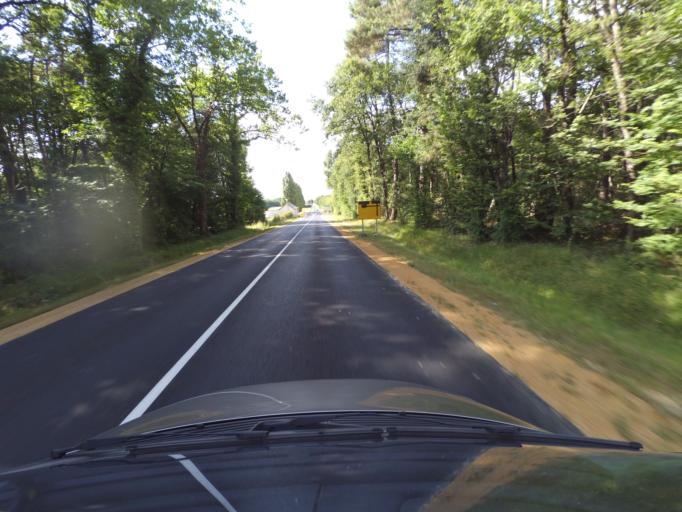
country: FR
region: Poitou-Charentes
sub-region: Departement de la Vienne
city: Saint-Gervais-les-Trois-Clochers
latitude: 46.9066
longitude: 0.4510
